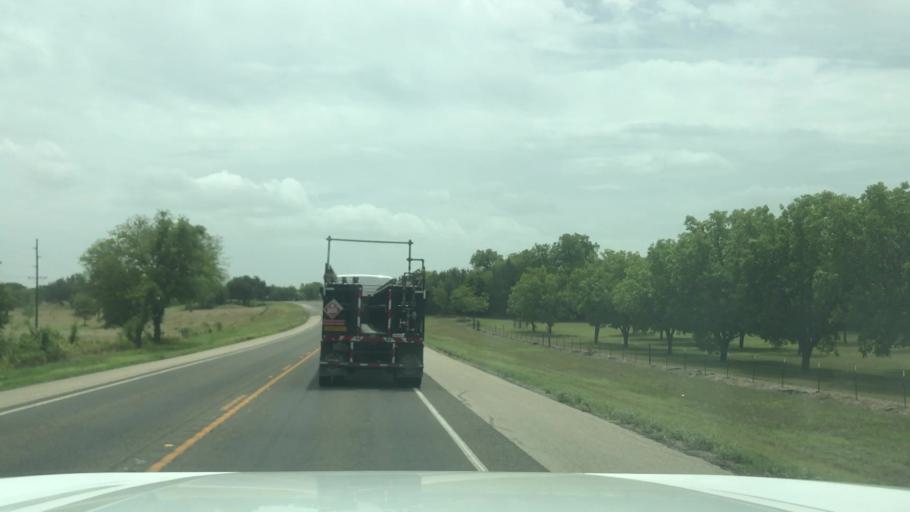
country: US
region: Texas
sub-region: Bosque County
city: Clifton
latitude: 31.7093
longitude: -97.5457
